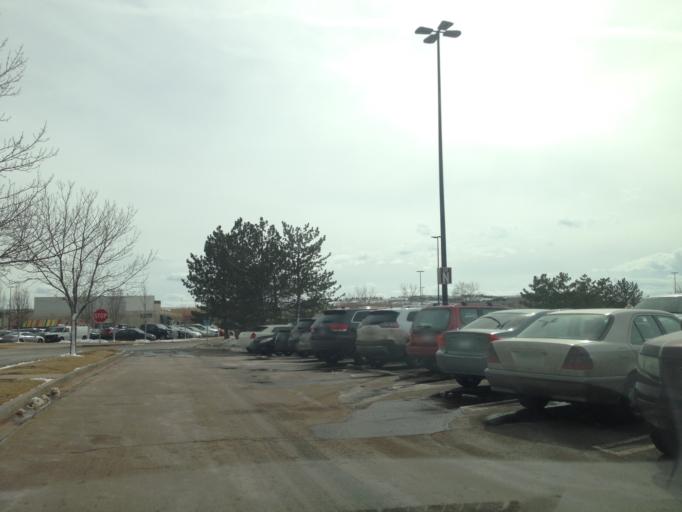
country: US
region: Colorado
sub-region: Boulder County
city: Superior
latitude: 39.9330
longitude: -105.1347
